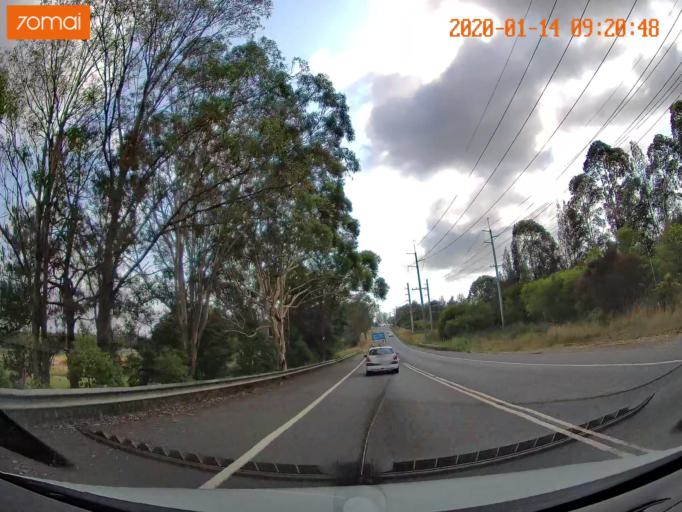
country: AU
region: New South Wales
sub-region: Lake Macquarie Shire
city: Dora Creek
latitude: -33.1145
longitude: 151.4732
